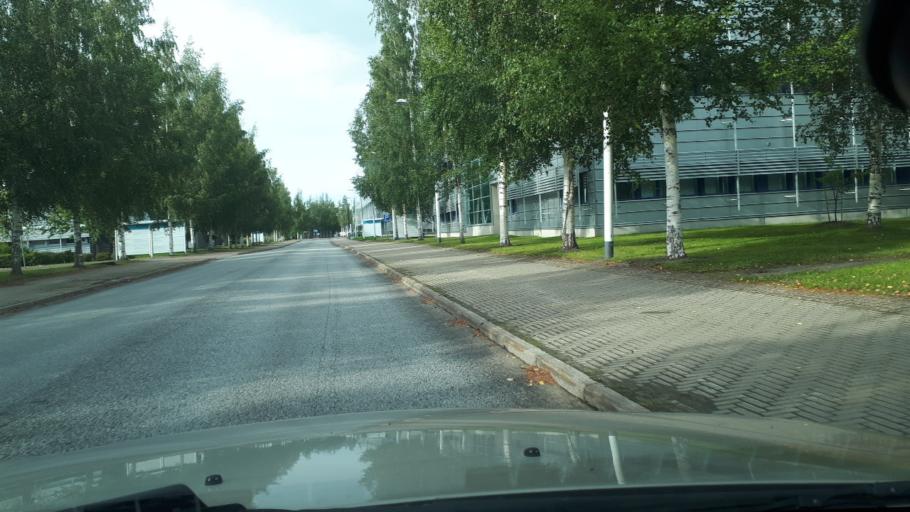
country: FI
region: Northern Ostrobothnia
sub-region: Oulu
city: Oulu
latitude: 65.0581
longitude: 25.4416
